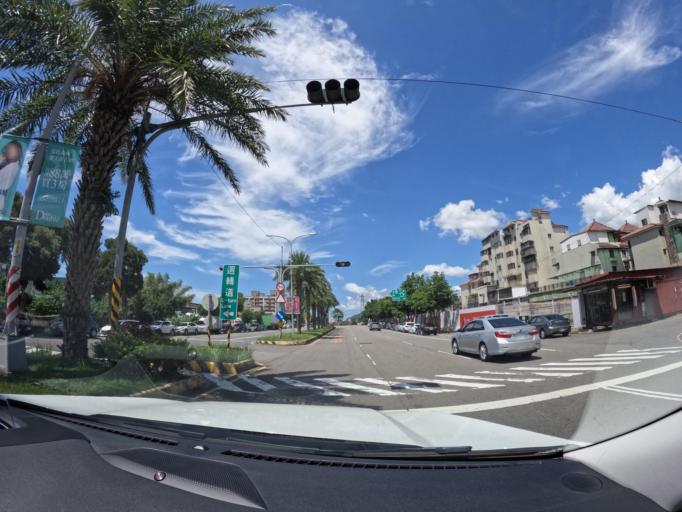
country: TW
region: Taipei
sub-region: Taipei
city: Banqiao
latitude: 25.0833
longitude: 121.3846
